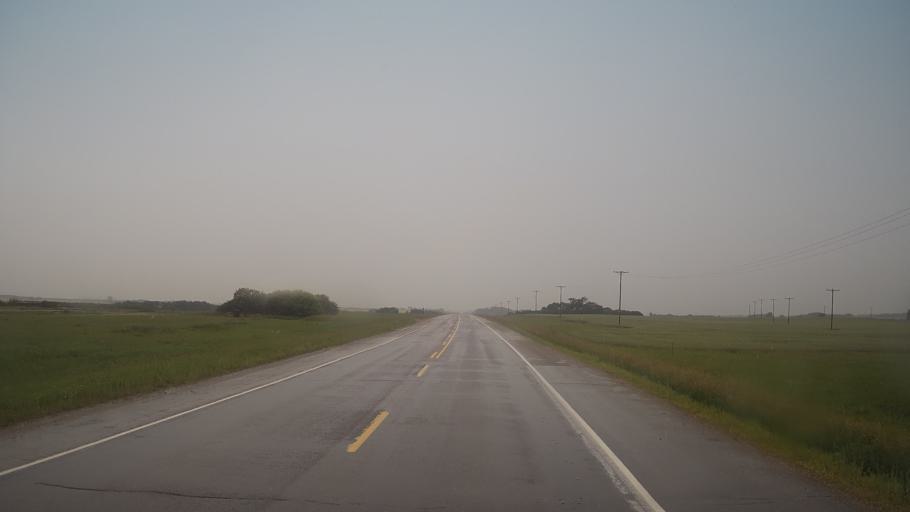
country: CA
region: Saskatchewan
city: Biggar
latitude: 52.1282
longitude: -108.1386
